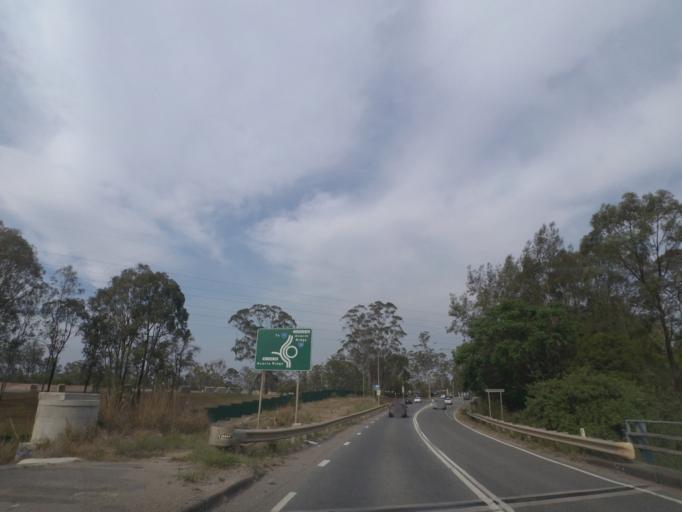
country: AU
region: Queensland
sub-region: Brisbane
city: Sunnybank
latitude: -27.5965
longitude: 153.0161
